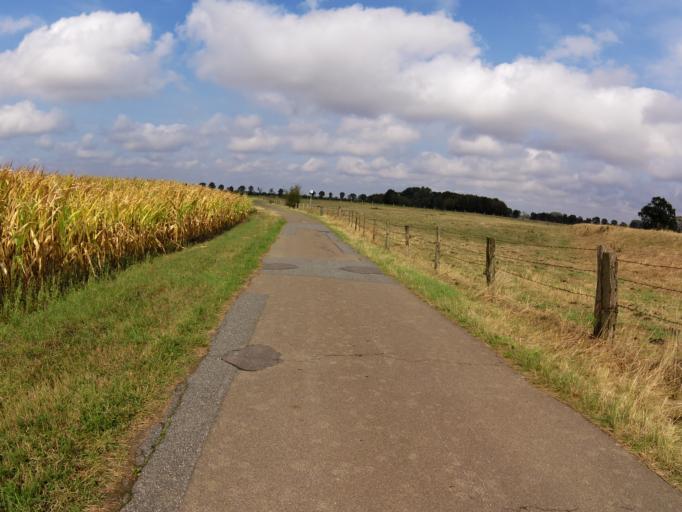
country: DE
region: Lower Saxony
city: Schweringen
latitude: 52.7568
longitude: 9.1783
